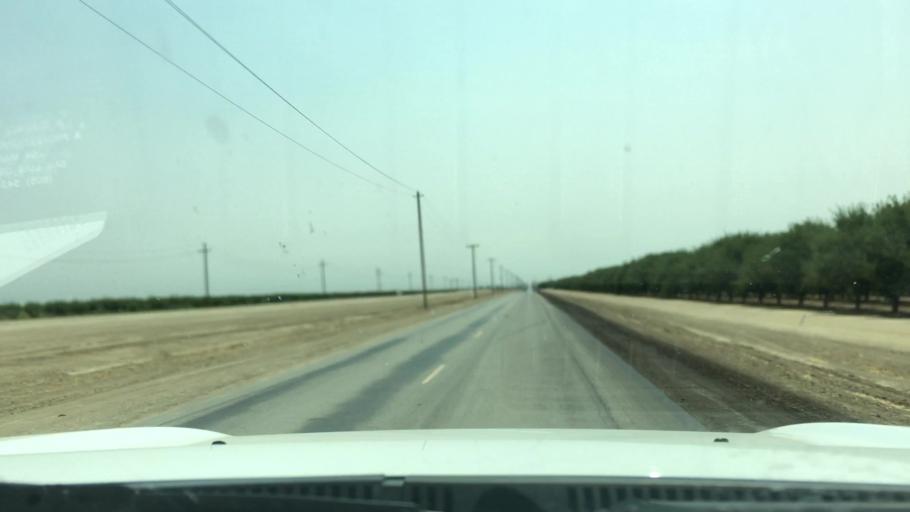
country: US
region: California
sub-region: Kern County
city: Wasco
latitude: 35.6297
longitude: -119.4377
